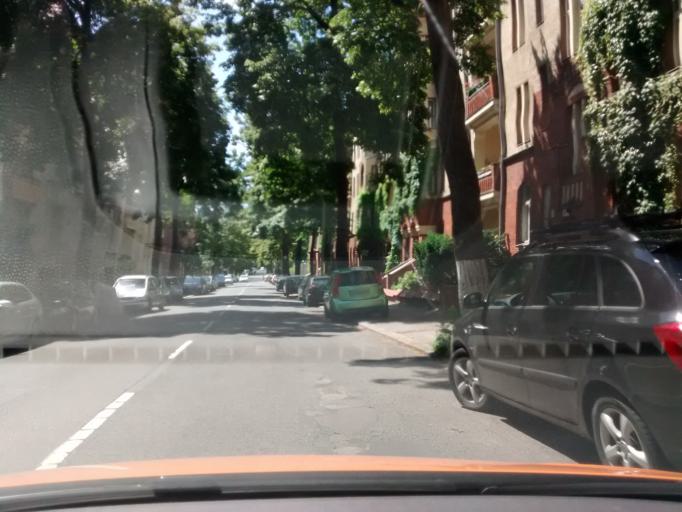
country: DE
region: Berlin
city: Steglitz Bezirk
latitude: 52.4510
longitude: 13.3294
